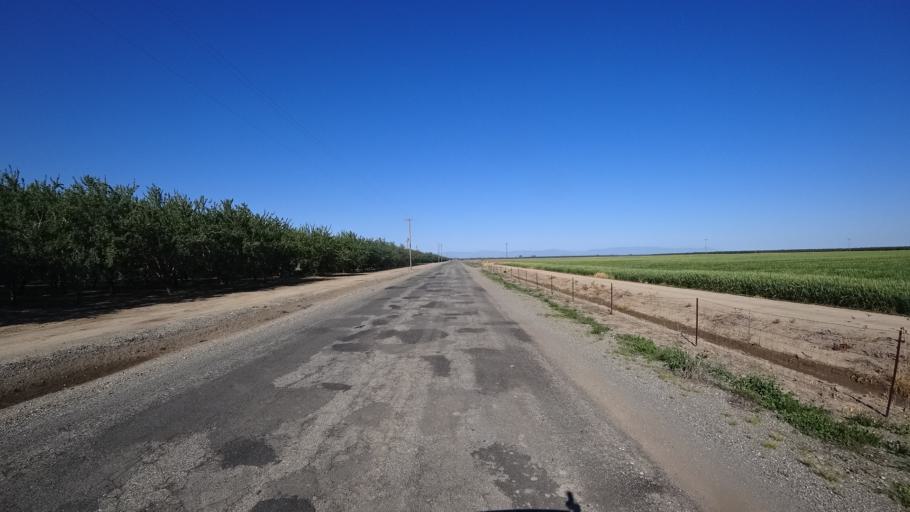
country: US
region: California
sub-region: Glenn County
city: Hamilton City
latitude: 39.6781
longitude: -122.0290
